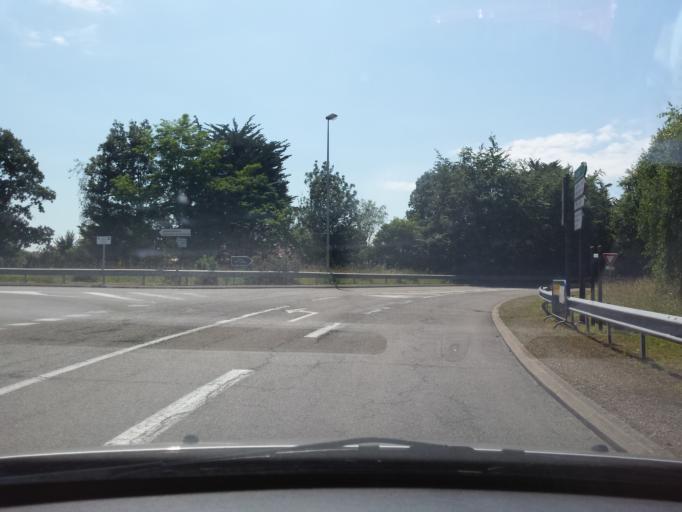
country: FR
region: Pays de la Loire
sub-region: Departement de la Loire-Atlantique
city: Pornic
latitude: 47.1217
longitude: -2.0974
